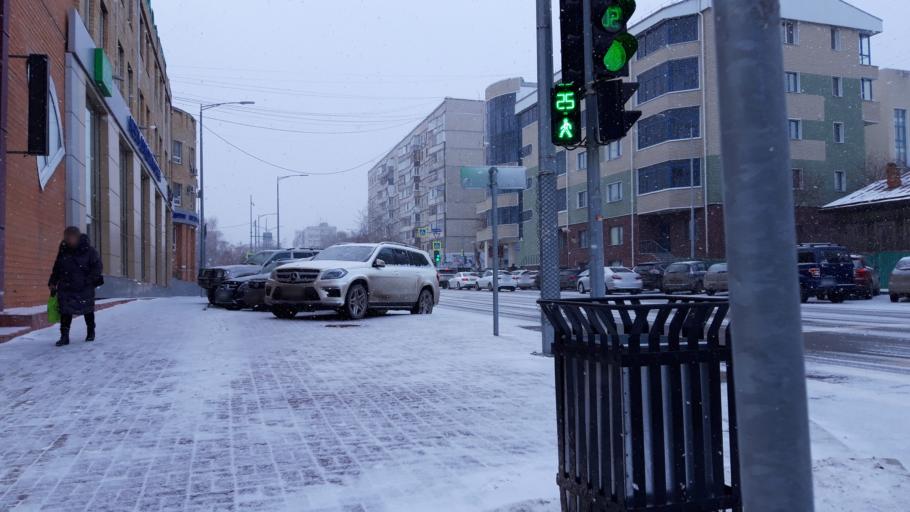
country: RU
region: Tjumen
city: Tyumen
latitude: 57.1589
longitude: 65.5520
